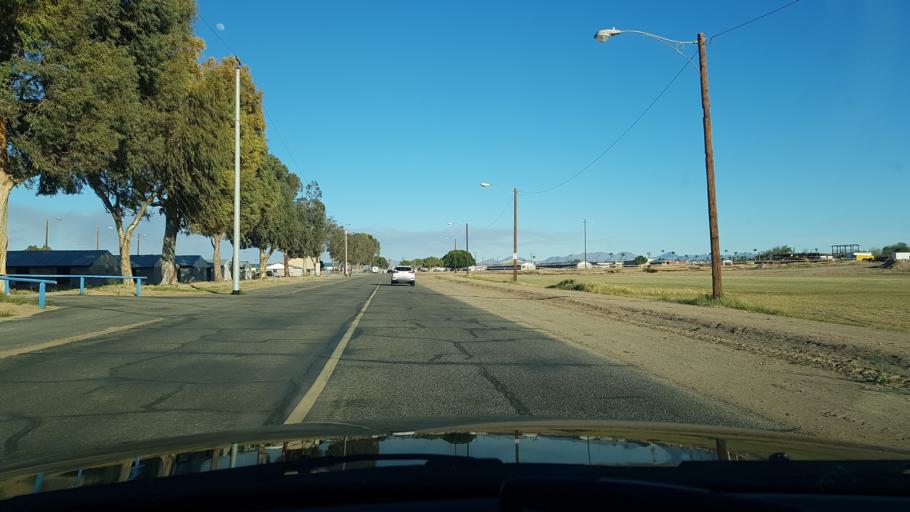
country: US
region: Arizona
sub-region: Yuma County
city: Yuma
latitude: 32.6730
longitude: -114.5969
